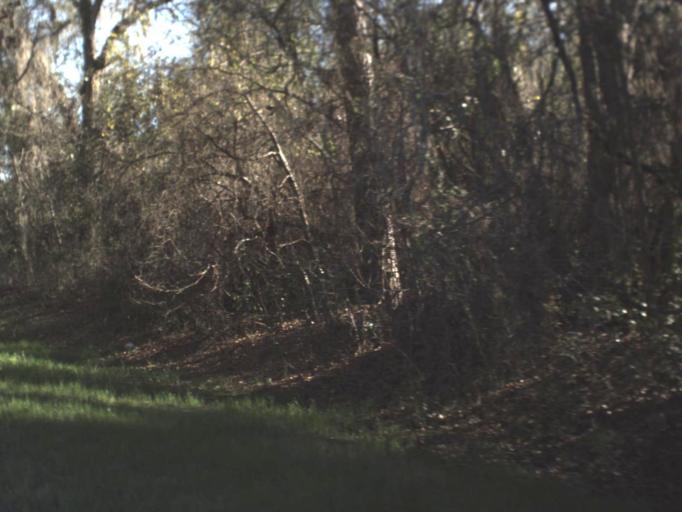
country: US
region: Georgia
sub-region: Brooks County
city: Quitman
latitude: 30.6540
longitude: -83.6420
